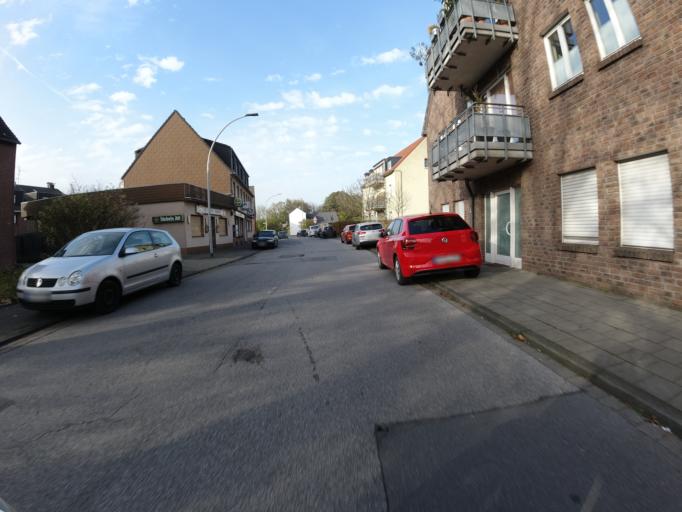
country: DE
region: North Rhine-Westphalia
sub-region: Regierungsbezirk Dusseldorf
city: Moers
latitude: 51.4024
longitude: 6.6648
